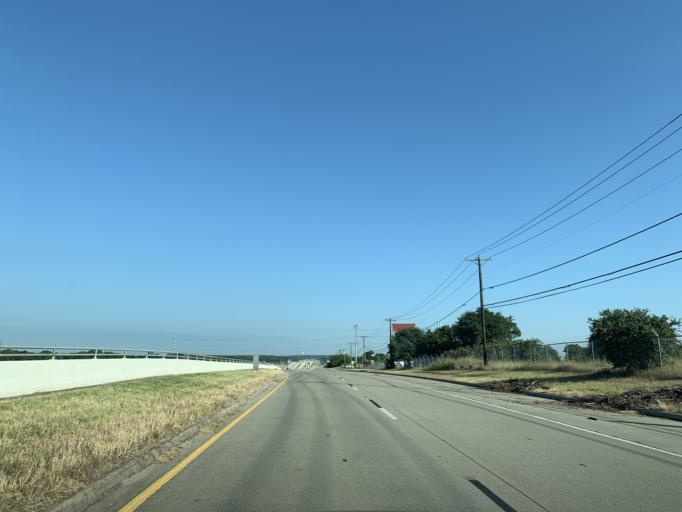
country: US
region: Texas
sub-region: Tarrant County
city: Lakeside
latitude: 32.8278
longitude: -97.4804
